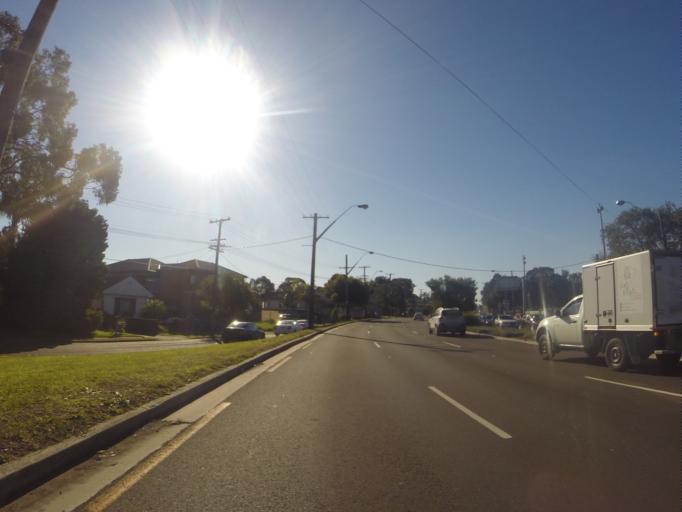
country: AU
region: New South Wales
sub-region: Canterbury
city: Lakemba
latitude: -33.9064
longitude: 151.0640
